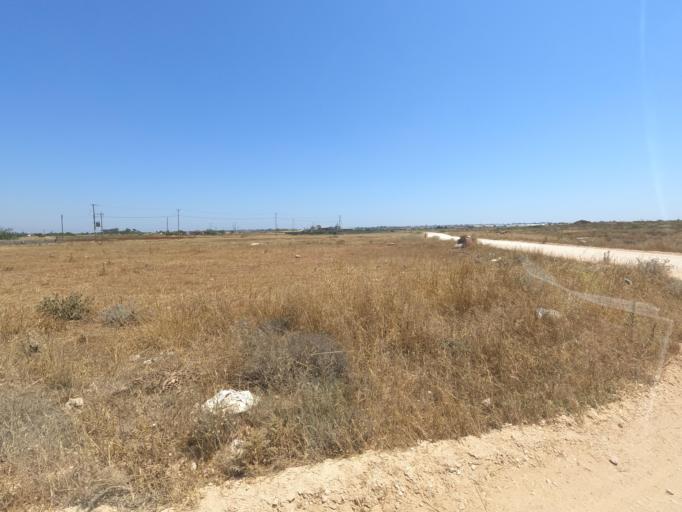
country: CY
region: Ammochostos
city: Liopetri
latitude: 35.0299
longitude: 33.8903
